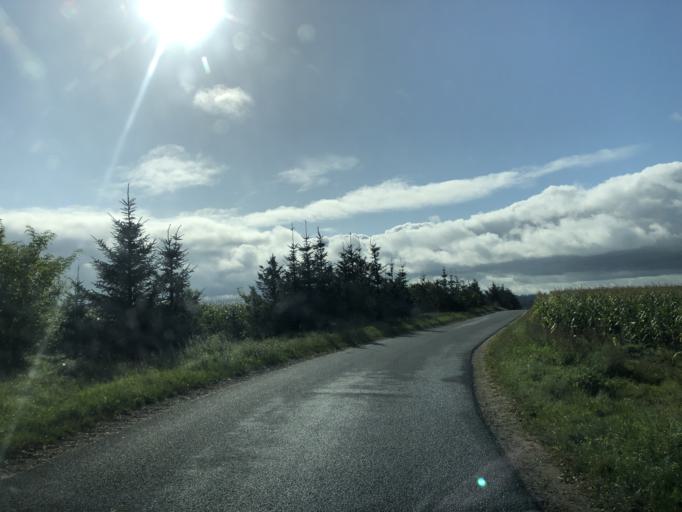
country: DK
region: Central Jutland
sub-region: Holstebro Kommune
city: Ulfborg
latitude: 56.3003
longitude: 8.4603
